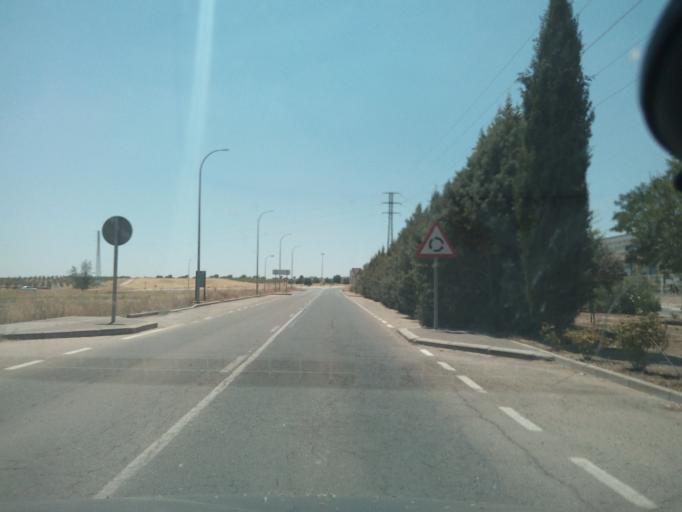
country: ES
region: Castille-La Mancha
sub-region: Province of Toledo
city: Villacanas
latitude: 39.6117
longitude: -3.3451
